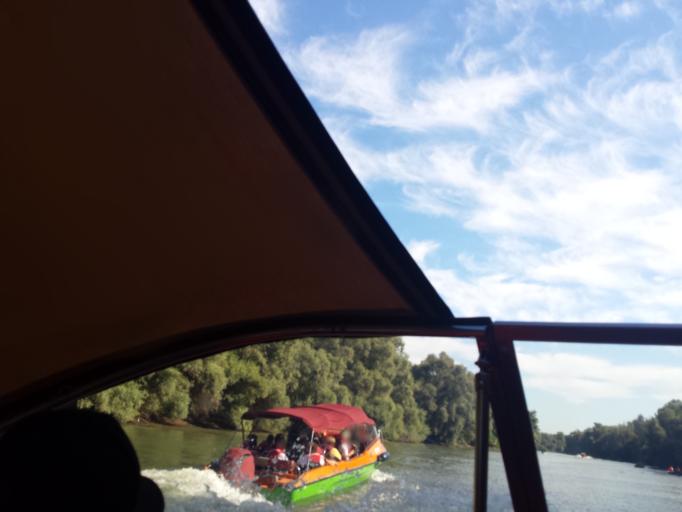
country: RO
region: Tulcea
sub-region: Comuna Nufaru
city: Nufaru
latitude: 45.2214
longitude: 28.8806
